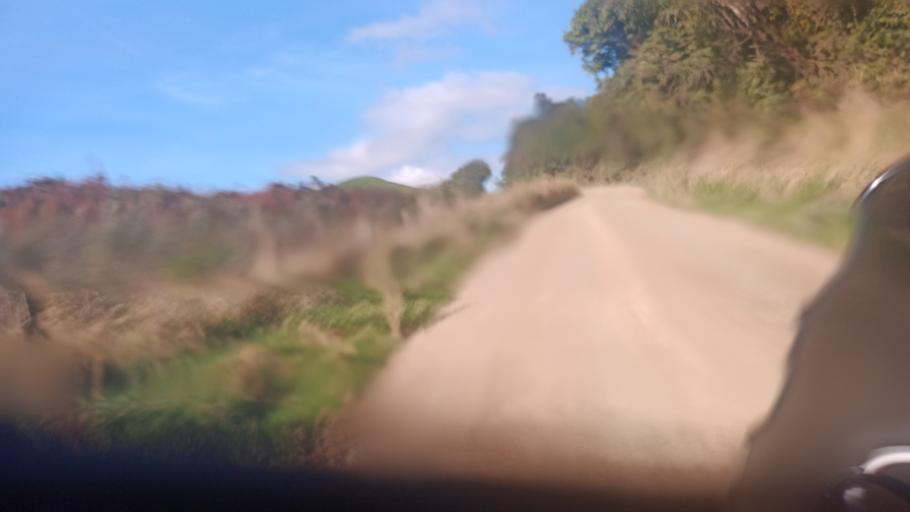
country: NZ
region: Bay of Plenty
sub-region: Opotiki District
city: Opotiki
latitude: -38.4233
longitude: 177.5590
